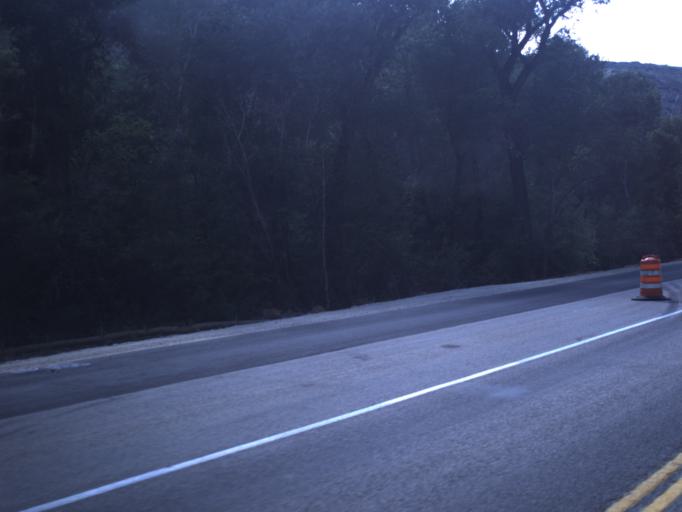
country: US
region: Utah
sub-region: Wasatch County
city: Heber
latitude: 40.4202
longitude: -111.3372
